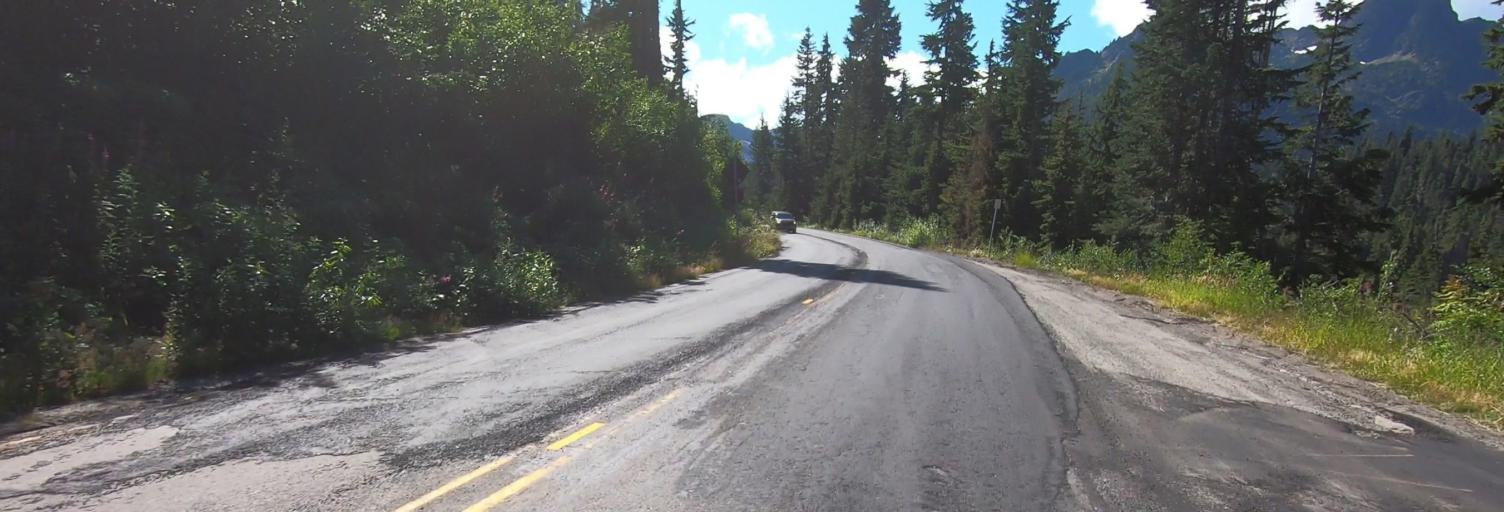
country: CA
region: British Columbia
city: Agassiz
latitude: 48.8645
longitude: -121.6651
